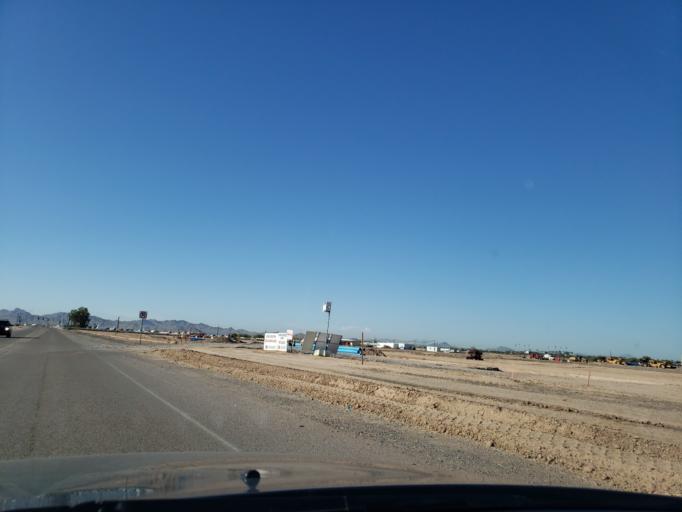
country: US
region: Arizona
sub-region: Maricopa County
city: Goodyear
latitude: 33.4394
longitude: -112.3755
